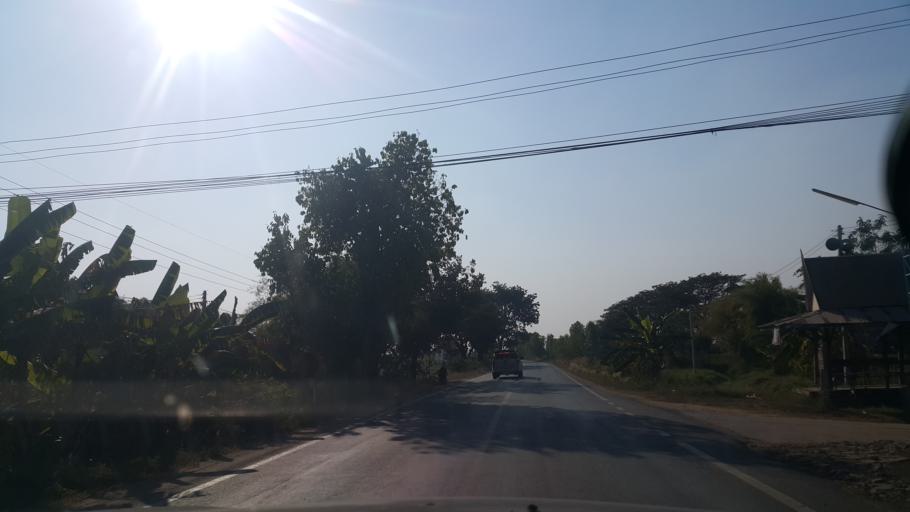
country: TH
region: Nakhon Ratchasima
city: Phimai
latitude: 15.1644
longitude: 102.3874
